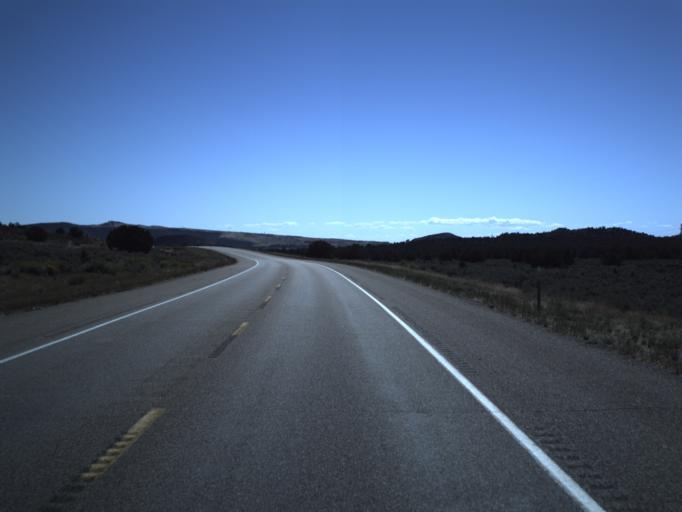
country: US
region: Utah
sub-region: Washington County
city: Ivins
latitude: 37.2789
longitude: -113.6516
